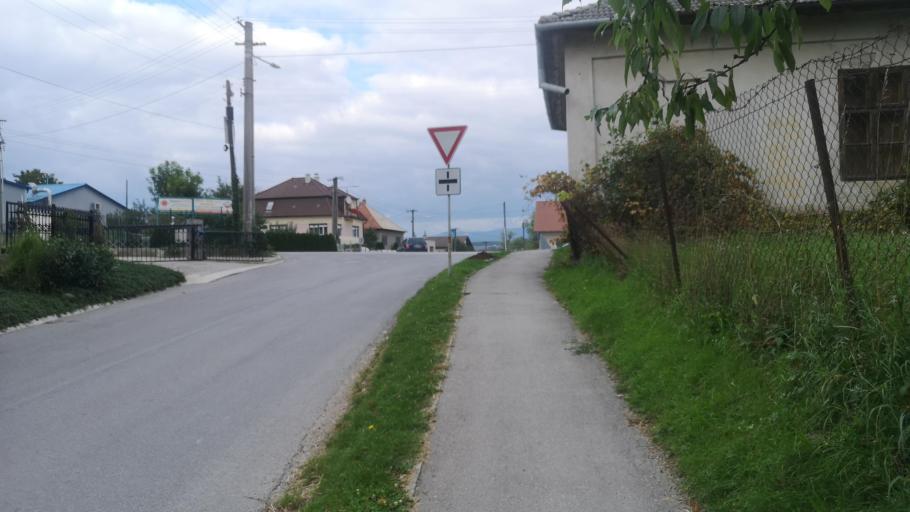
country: SK
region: Nitriansky
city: Banovce nad Bebravou
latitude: 48.7376
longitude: 18.2363
